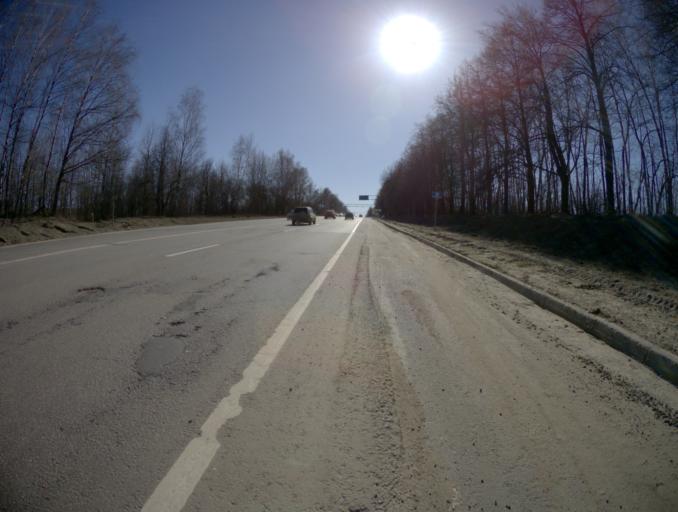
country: RU
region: Vladimir
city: Bogolyubovo
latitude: 56.1785
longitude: 40.5031
